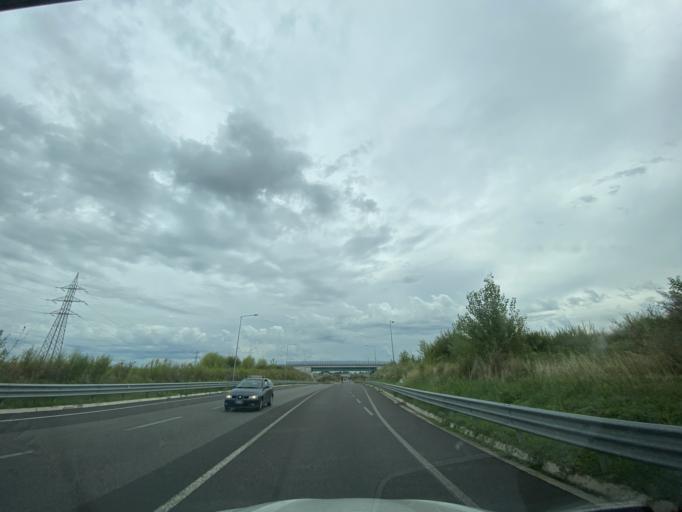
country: IT
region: Lombardy
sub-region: Provincia di Monza e Brianza
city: Caponago
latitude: 45.5601
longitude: 9.3817
